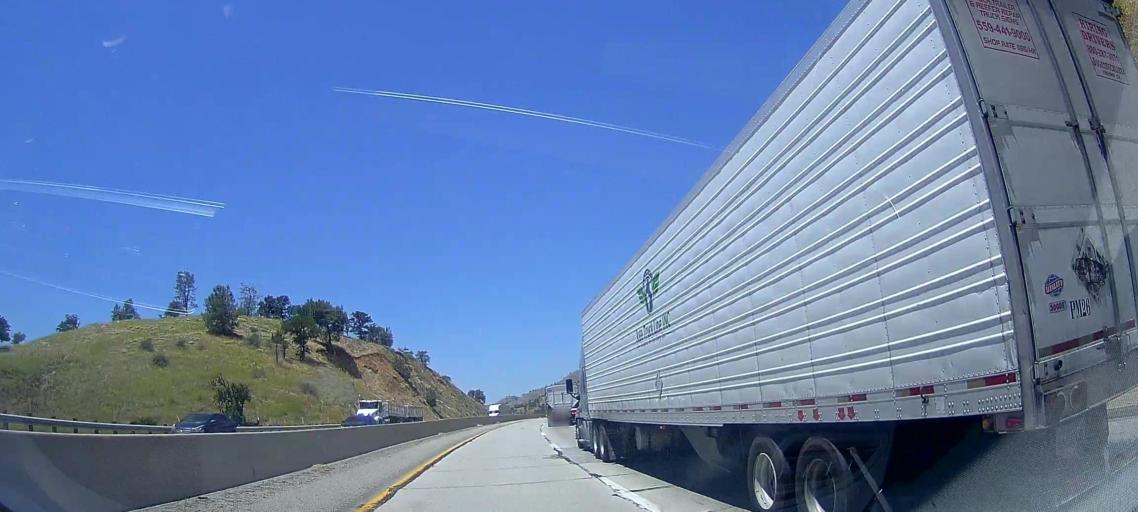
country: US
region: California
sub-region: Kern County
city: Golden Hills
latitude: 35.1869
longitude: -118.5039
